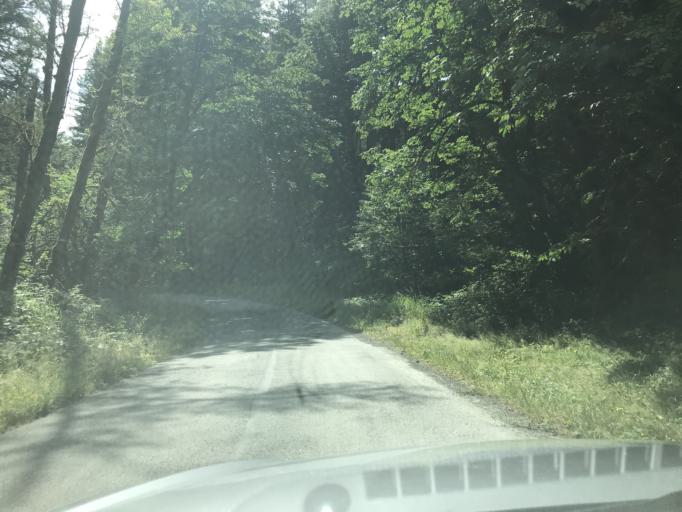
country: US
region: Washington
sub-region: King County
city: Hobart
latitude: 47.4164
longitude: -121.9195
